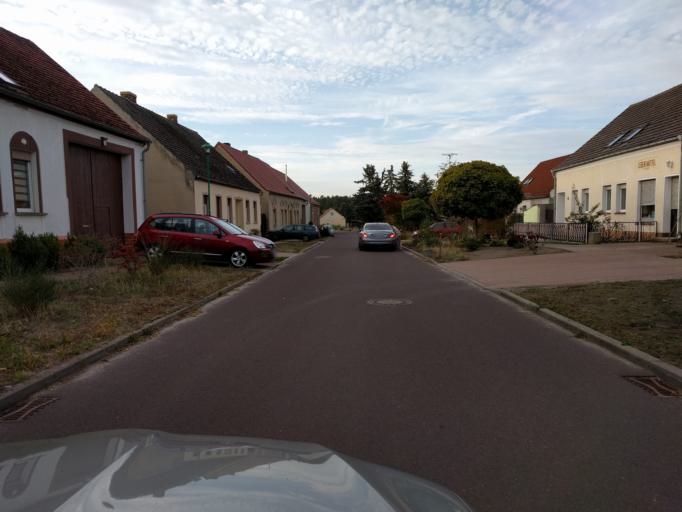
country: DE
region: Brandenburg
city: Ziesar
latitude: 52.2136
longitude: 12.2839
